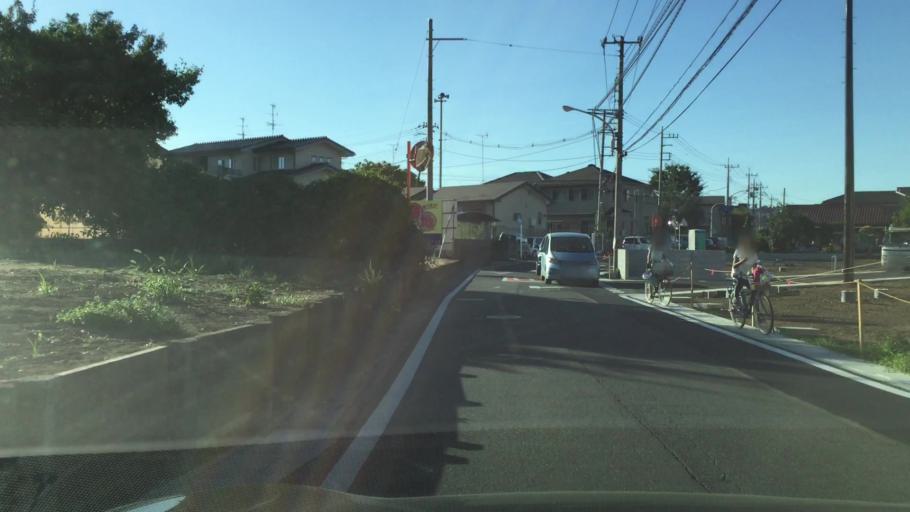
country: JP
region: Saitama
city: Ageoshimo
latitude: 35.9208
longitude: 139.5862
